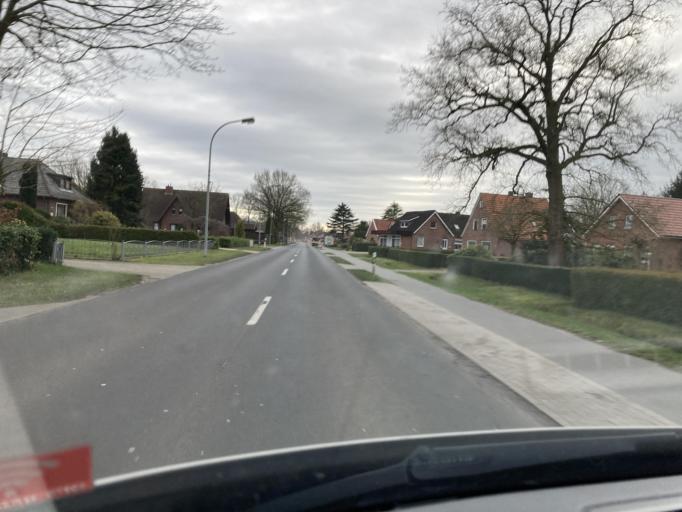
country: DE
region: Lower Saxony
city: Papenburg
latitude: 53.1373
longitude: 7.4758
